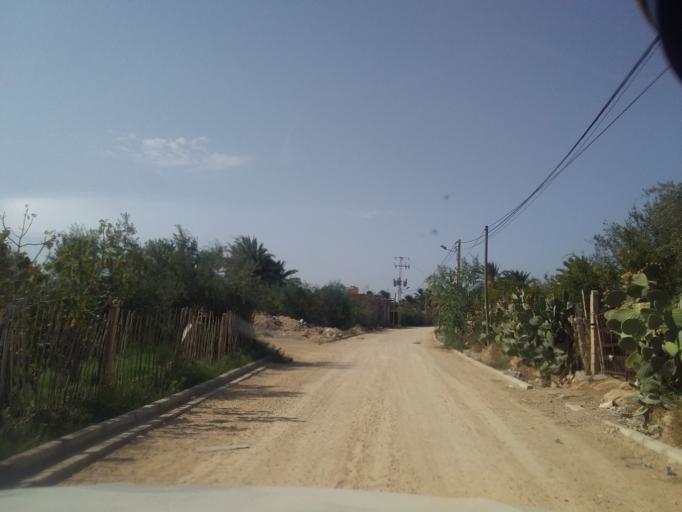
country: TN
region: Qabis
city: Gabes
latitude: 33.6239
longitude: 10.2851
